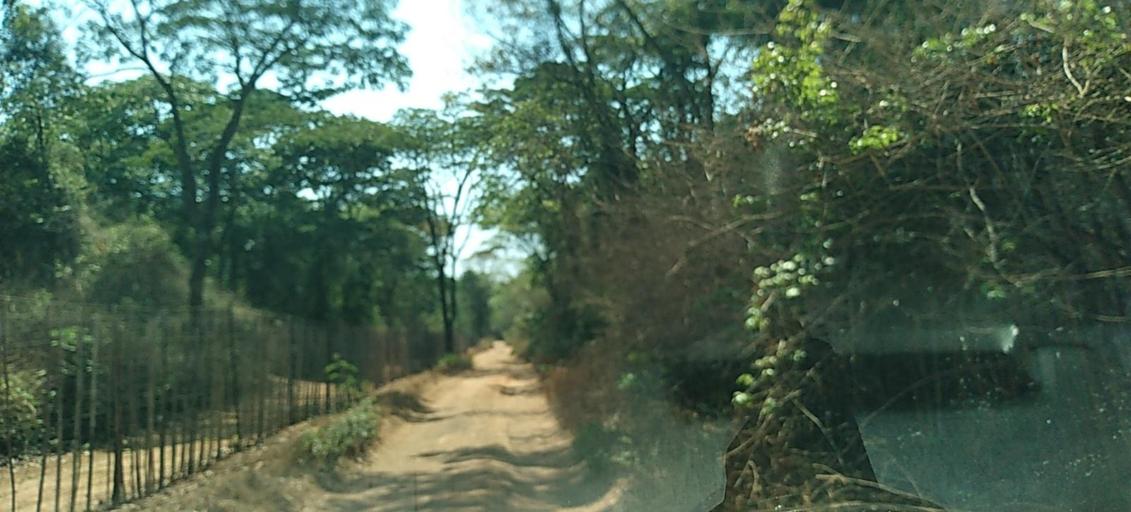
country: ZM
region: Copperbelt
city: Luanshya
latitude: -13.0086
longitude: 28.4556
